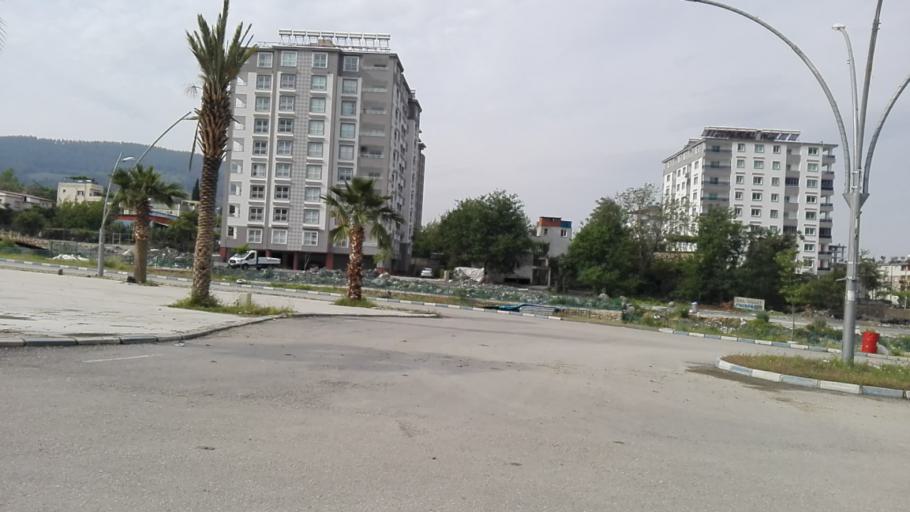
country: TR
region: Osmaniye
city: Haruniye
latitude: 37.2491
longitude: 36.4662
